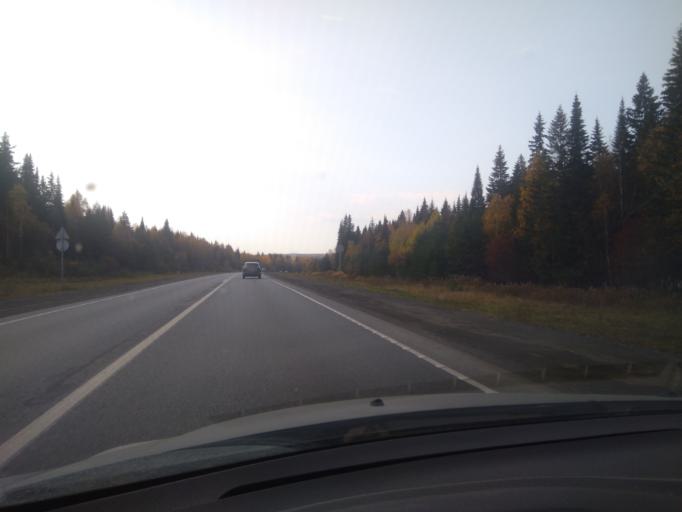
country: RU
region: Sverdlovsk
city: Druzhinino
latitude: 56.8152
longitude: 59.5607
